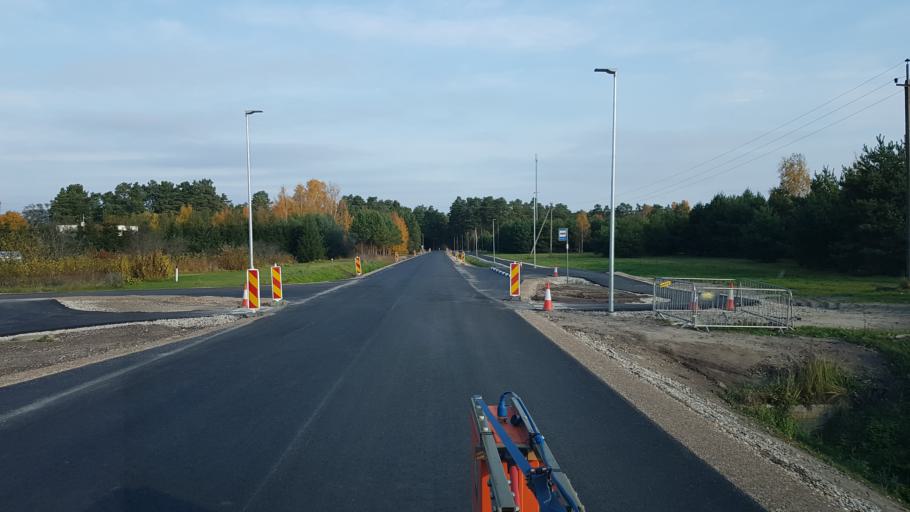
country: EE
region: Paernumaa
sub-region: Paikuse vald
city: Paikuse
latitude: 58.3438
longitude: 24.6205
